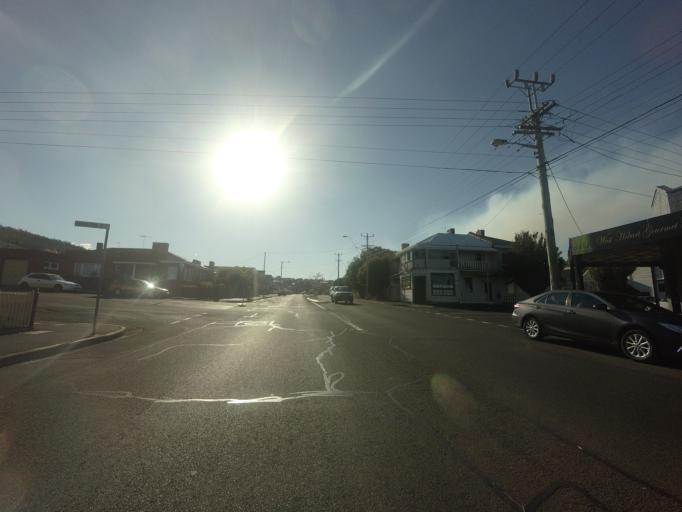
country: AU
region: Tasmania
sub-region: Hobart
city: Hobart
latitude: -42.8788
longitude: 147.3106
